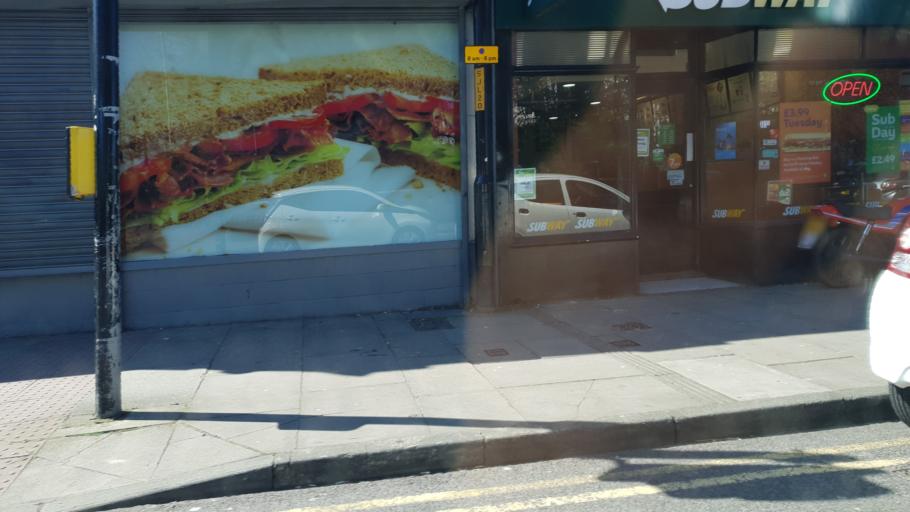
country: GB
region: England
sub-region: Middlesbrough
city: Middlesbrough
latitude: 54.5570
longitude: -1.2476
